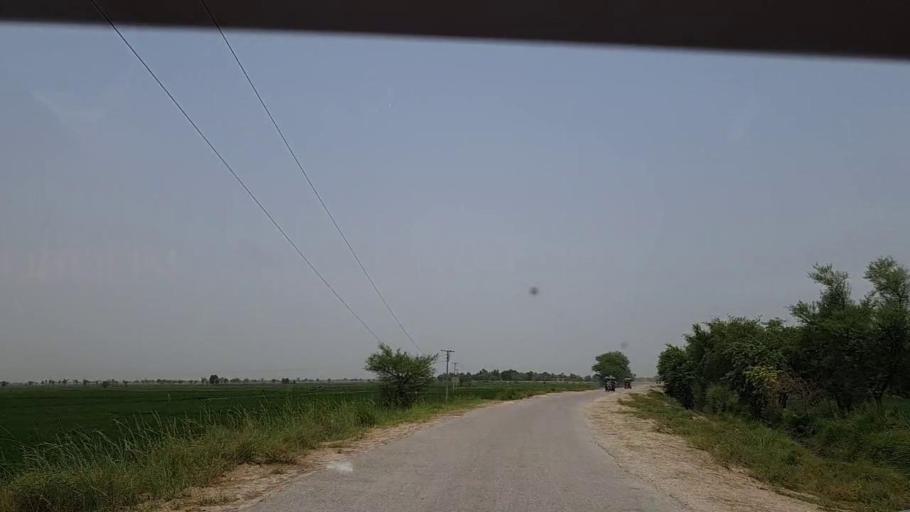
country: PK
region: Sindh
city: Khairpur Nathan Shah
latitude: 27.0094
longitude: 67.6700
